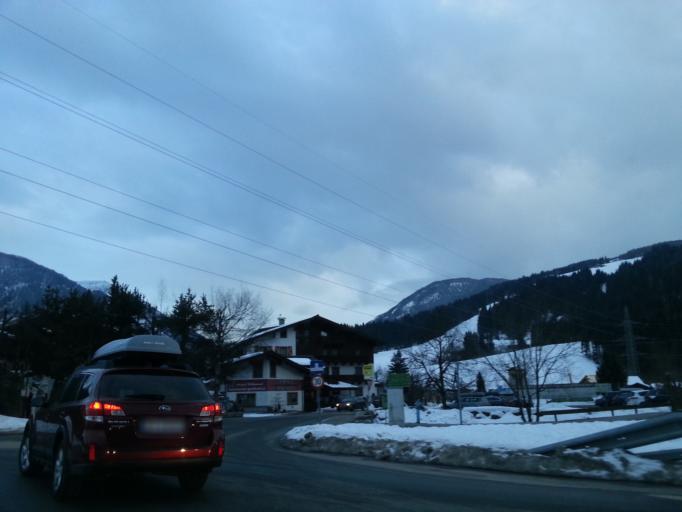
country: AT
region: Salzburg
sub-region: Politischer Bezirk Sankt Johann im Pongau
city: Flachau
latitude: 47.3622
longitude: 13.3820
